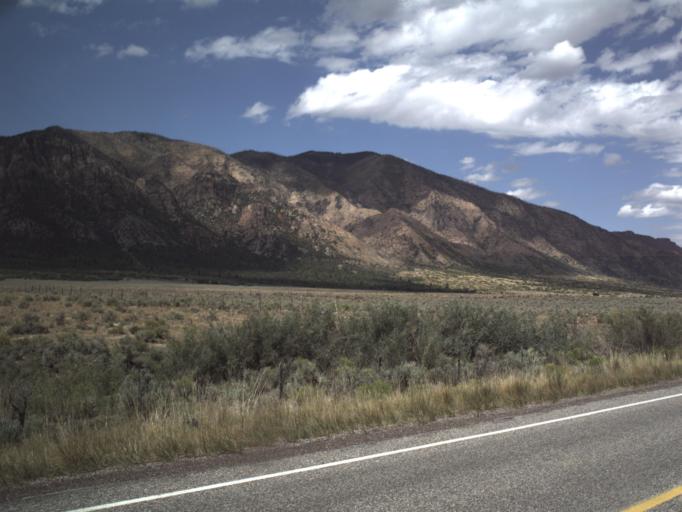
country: US
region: Utah
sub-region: Sanpete County
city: Centerfield
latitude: 39.1331
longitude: -112.0592
